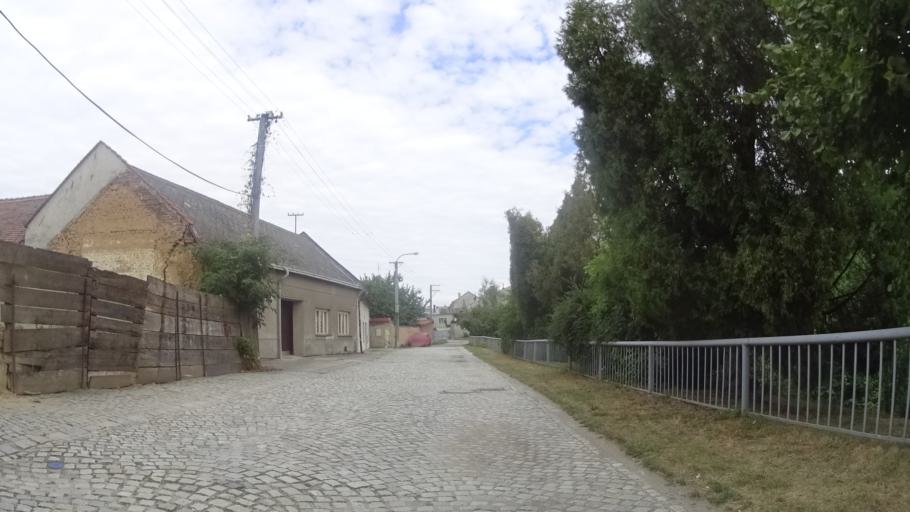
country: CZ
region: Olomoucky
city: Tovacov
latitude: 49.4284
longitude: 17.2902
